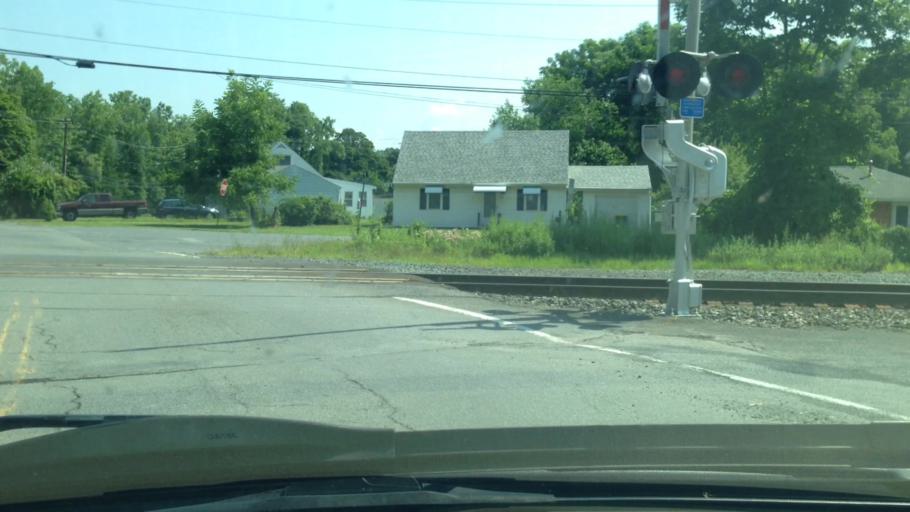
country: US
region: New York
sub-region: Ulster County
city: Port Ewen
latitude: 41.8988
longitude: -73.9889
